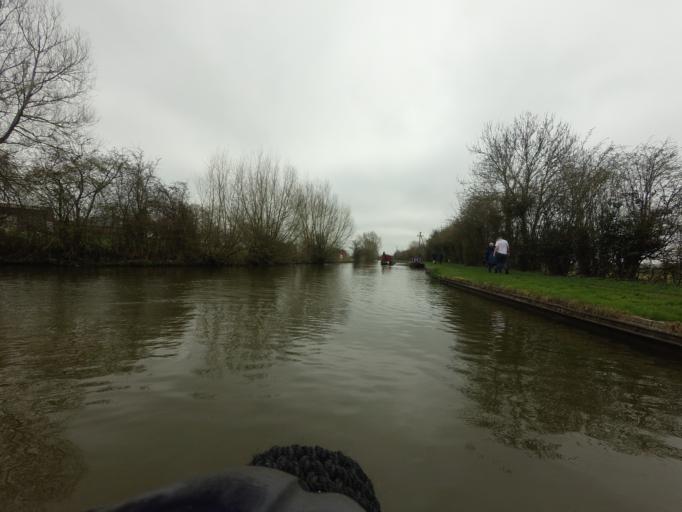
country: GB
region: England
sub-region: Buckinghamshire
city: Cheddington
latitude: 51.8726
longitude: -0.6505
